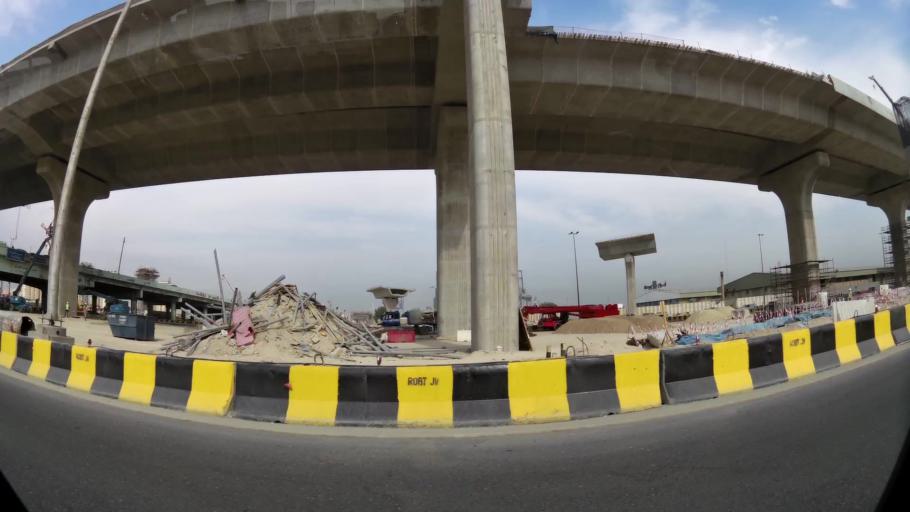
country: KW
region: Al Asimah
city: Ash Shamiyah
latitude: 29.3400
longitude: 47.9263
